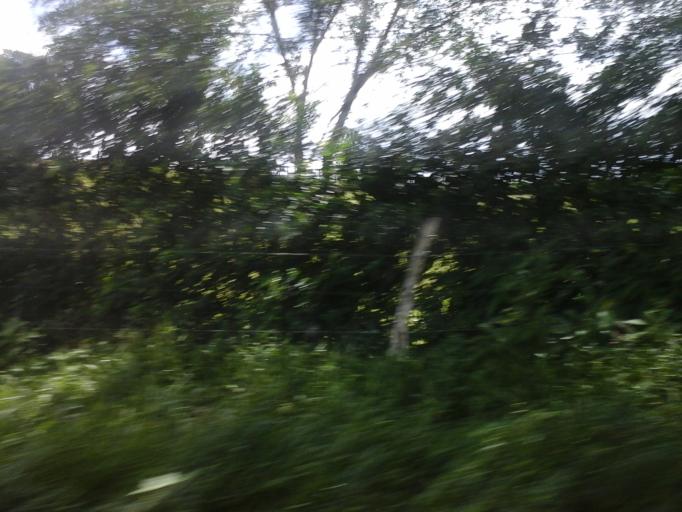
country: CO
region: Caqueta
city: El Doncello
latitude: 1.6075
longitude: -75.0022
